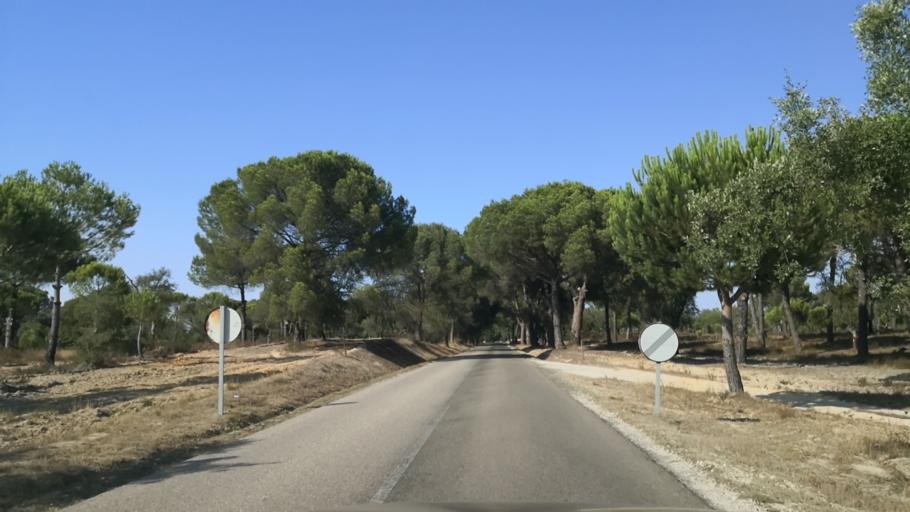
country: PT
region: Santarem
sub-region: Coruche
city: Coruche
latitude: 38.8364
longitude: -8.5584
